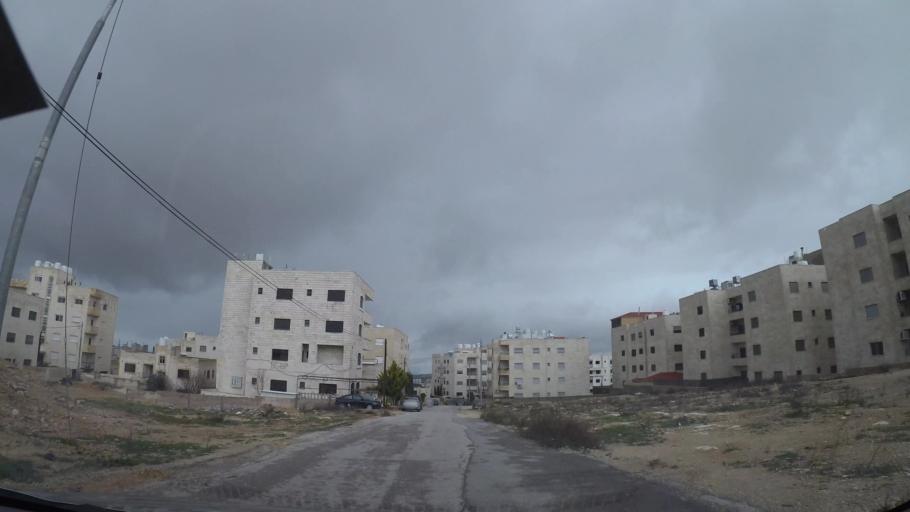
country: JO
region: Amman
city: Al Jubayhah
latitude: 32.0591
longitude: 35.8881
